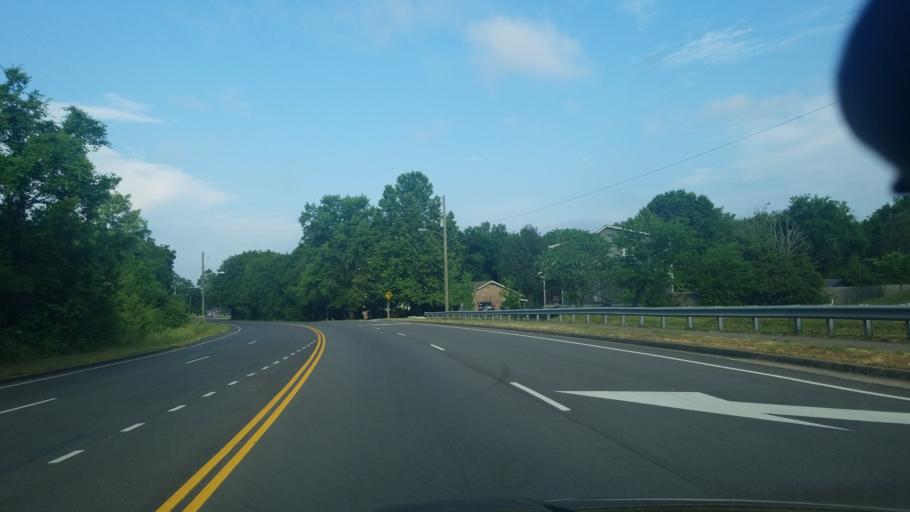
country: US
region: Tennessee
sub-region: Davidson County
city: Nashville
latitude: 36.2310
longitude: -86.7518
